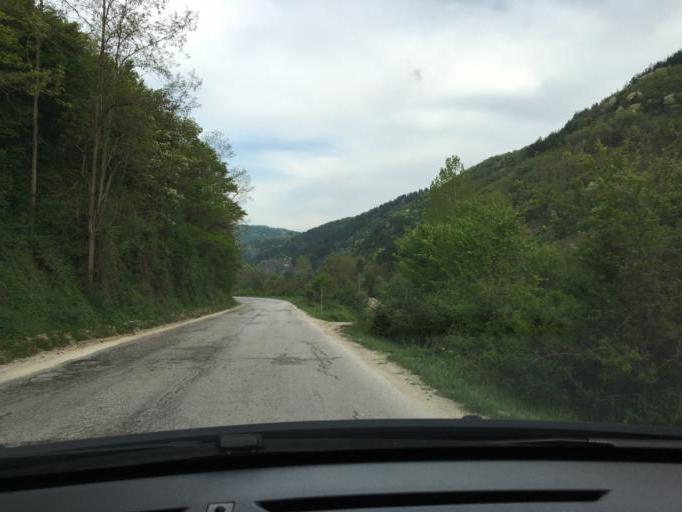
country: MK
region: Kriva Palanka
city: Kriva Palanka
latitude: 42.2259
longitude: 22.3881
